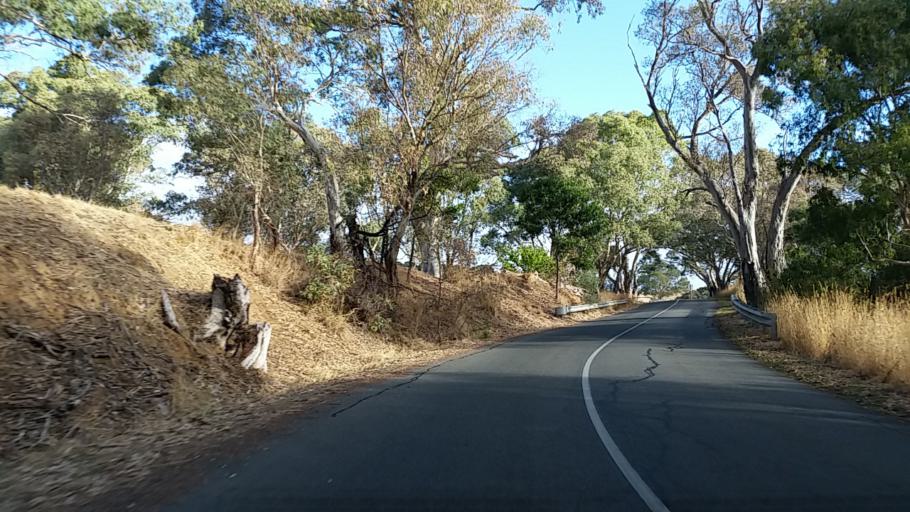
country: AU
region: South Australia
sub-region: Yankalilla
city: Normanville
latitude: -35.5074
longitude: 138.2619
